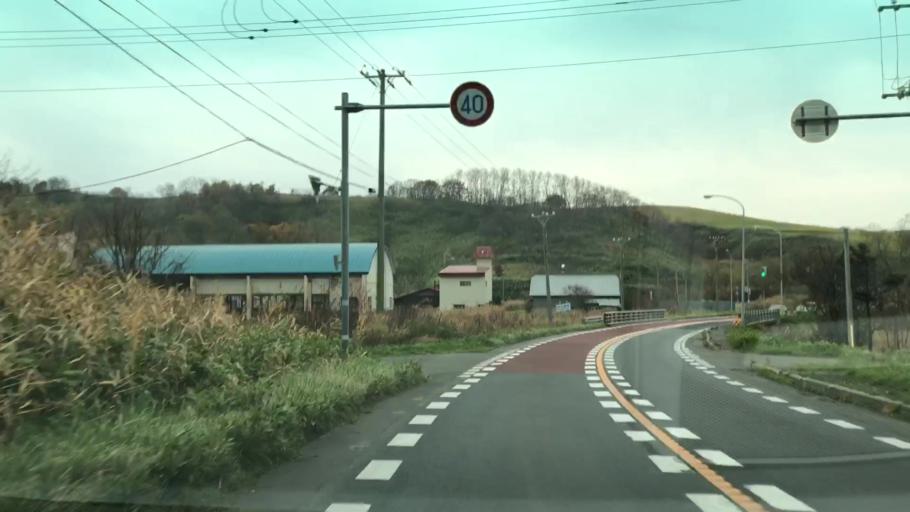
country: JP
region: Hokkaido
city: Ishikari
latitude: 43.3563
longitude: 141.4304
